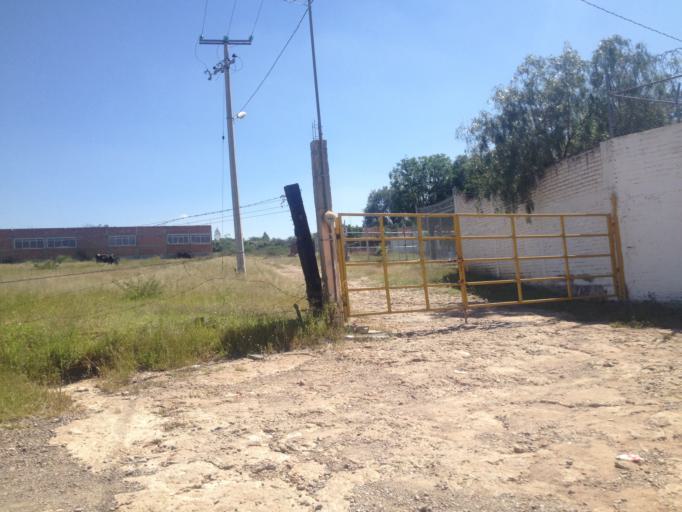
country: MX
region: Aguascalientes
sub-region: Aguascalientes
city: San Sebastian [Fraccionamiento]
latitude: 21.7883
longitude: -102.2624
